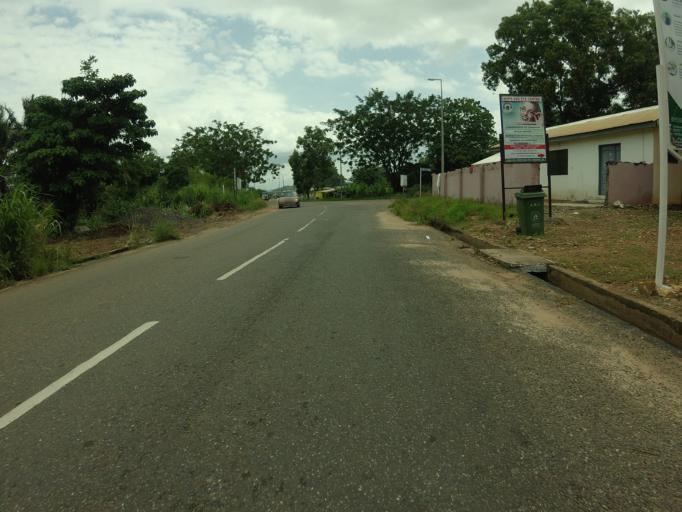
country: GH
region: Volta
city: Ho
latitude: 6.5935
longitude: 0.4635
